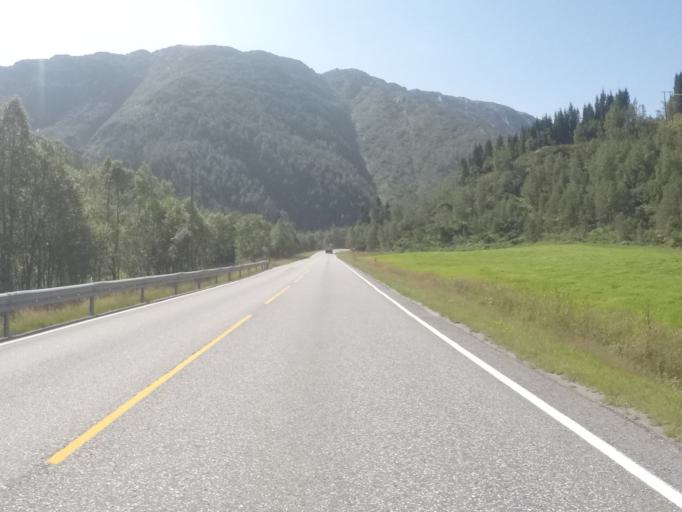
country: NO
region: Hordaland
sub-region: Odda
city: Odda
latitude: 59.9193
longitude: 6.5652
